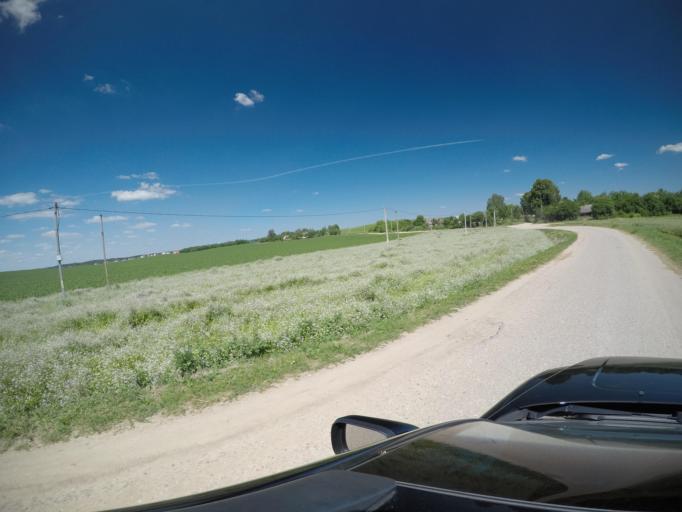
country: BY
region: Grodnenskaya
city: Hrodna
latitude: 53.7296
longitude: 23.8512
